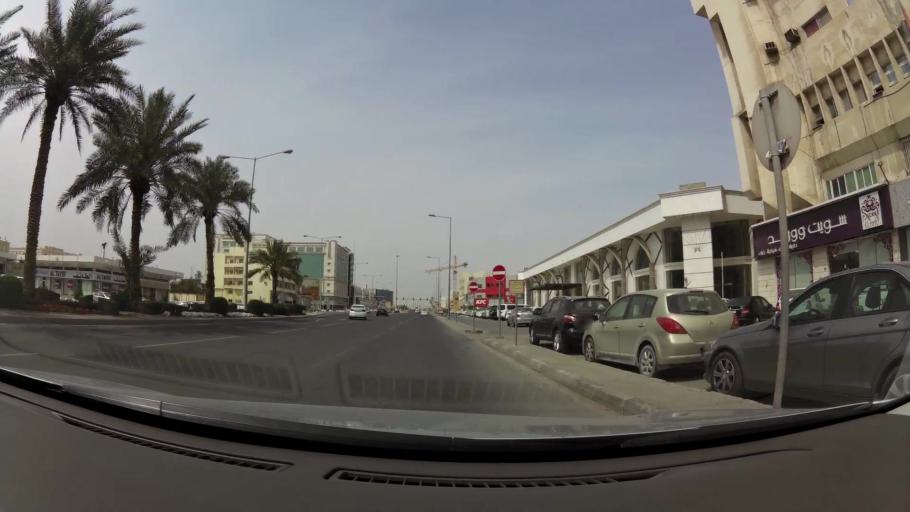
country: QA
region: Baladiyat ad Dawhah
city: Doha
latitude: 25.2810
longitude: 51.5002
